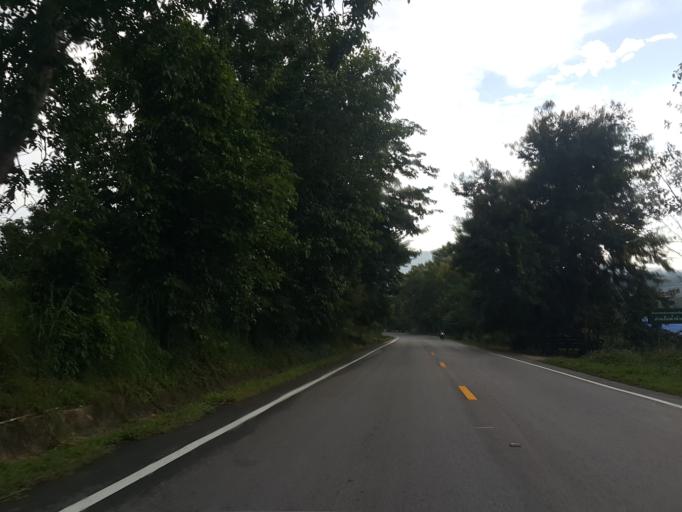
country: TH
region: Chiang Mai
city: Phrao
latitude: 19.2572
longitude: 99.1860
